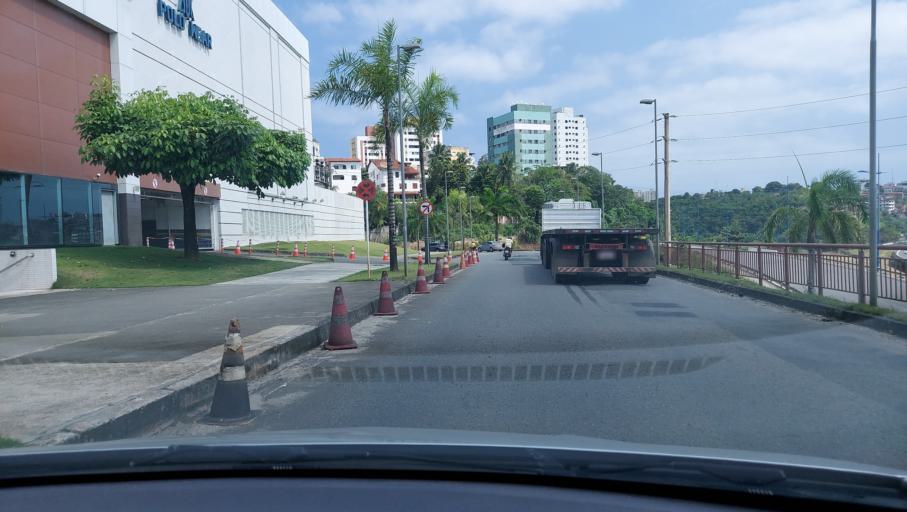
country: BR
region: Bahia
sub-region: Salvador
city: Salvador
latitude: -12.9712
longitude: -38.4750
